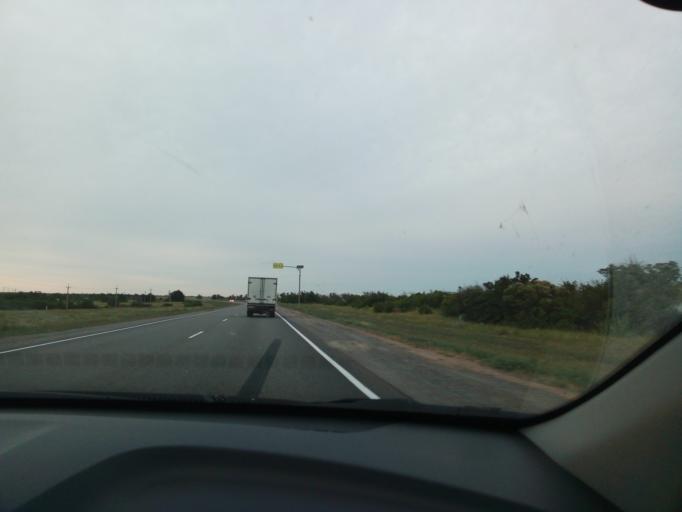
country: RU
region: Volgograd
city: Primorsk
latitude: 49.2144
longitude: 44.9052
